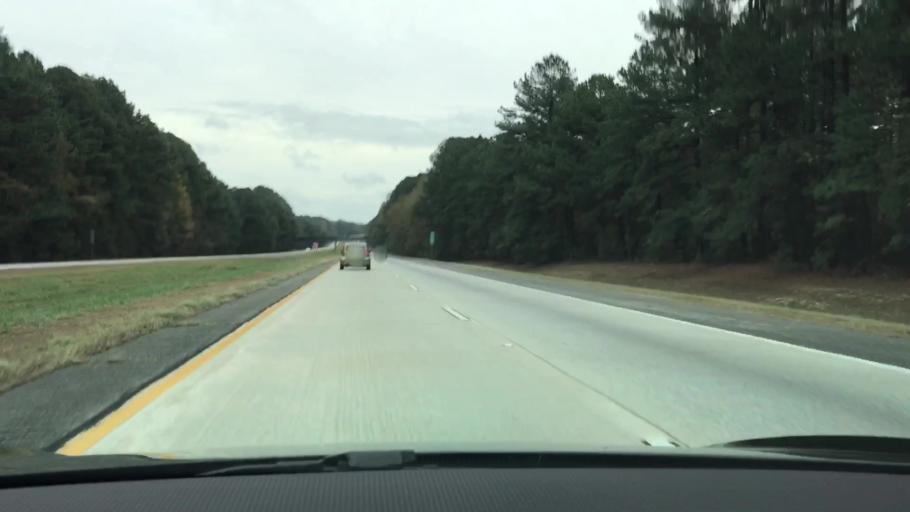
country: US
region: Georgia
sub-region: Greene County
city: Union Point
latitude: 33.5491
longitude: -83.0491
